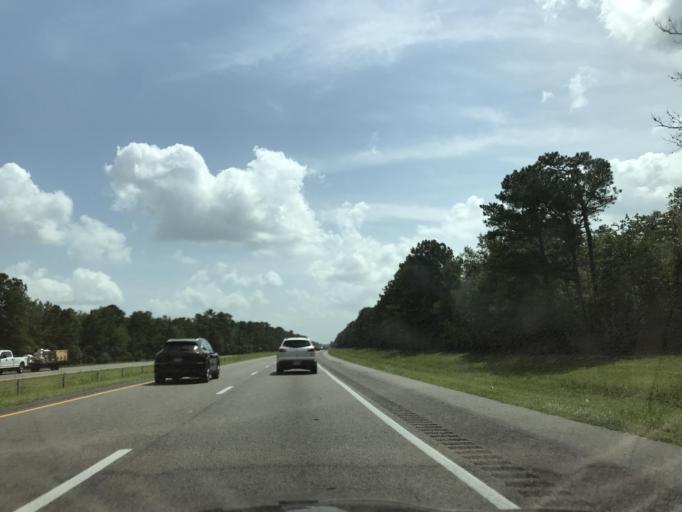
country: US
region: North Carolina
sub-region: Pender County
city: Rocky Point
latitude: 34.5017
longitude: -77.8768
